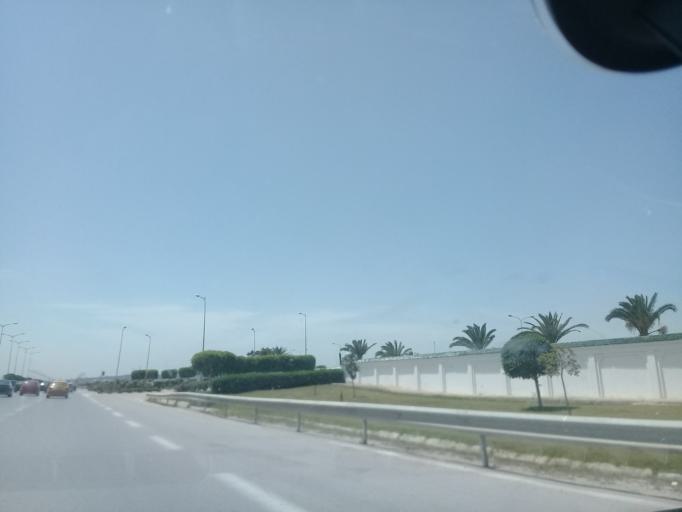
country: TN
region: Ariana
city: Ariana
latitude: 36.8371
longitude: 10.2289
